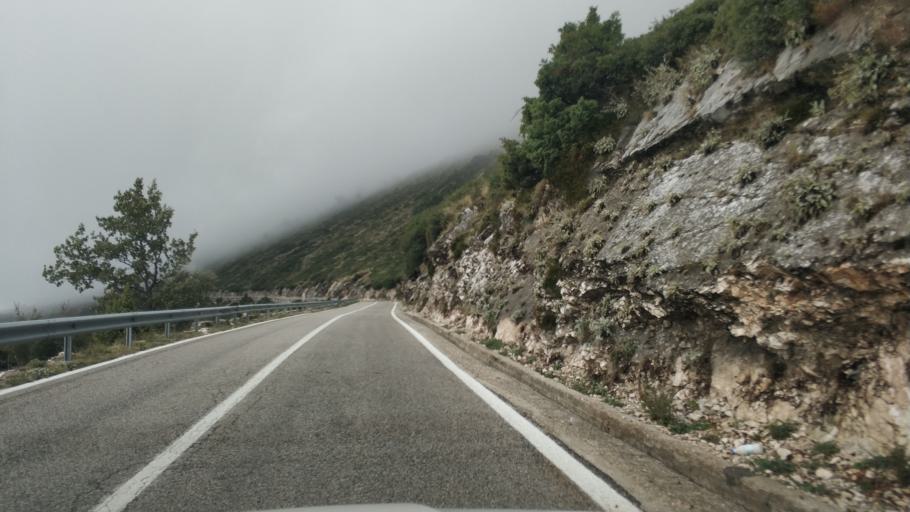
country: AL
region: Vlore
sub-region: Rrethi i Vlores
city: Vranisht
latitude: 40.1907
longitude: 19.6066
